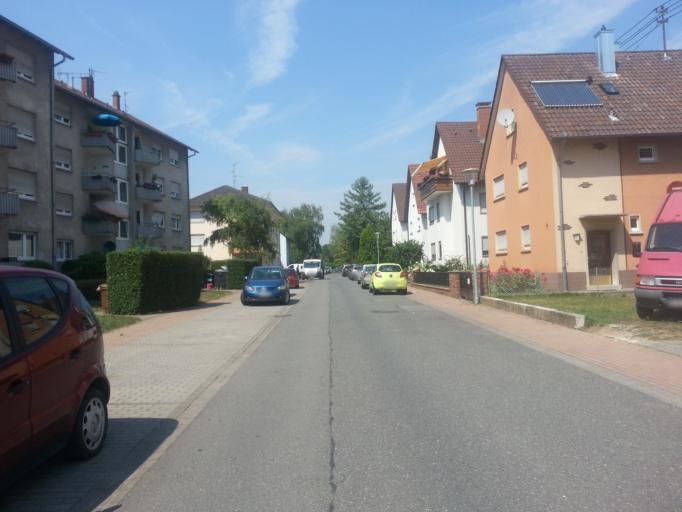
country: DE
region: Baden-Wuerttemberg
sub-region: Karlsruhe Region
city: Edingen-Neckarhausen
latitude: 49.4489
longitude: 8.6041
